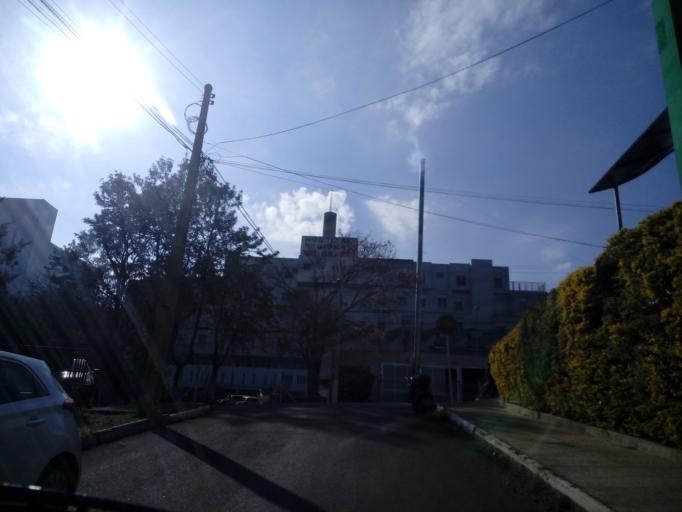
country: BR
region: Santa Catarina
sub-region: Chapeco
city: Chapeco
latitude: -27.1087
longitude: -52.5994
